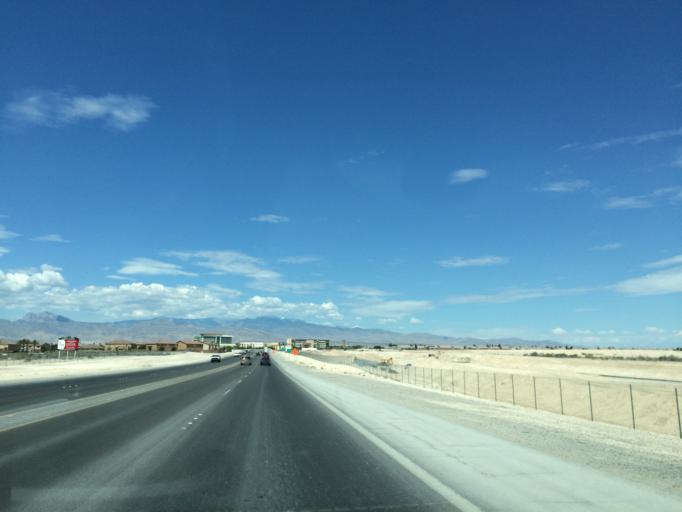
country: US
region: Nevada
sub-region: Clark County
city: North Las Vegas
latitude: 36.2928
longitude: -115.1624
